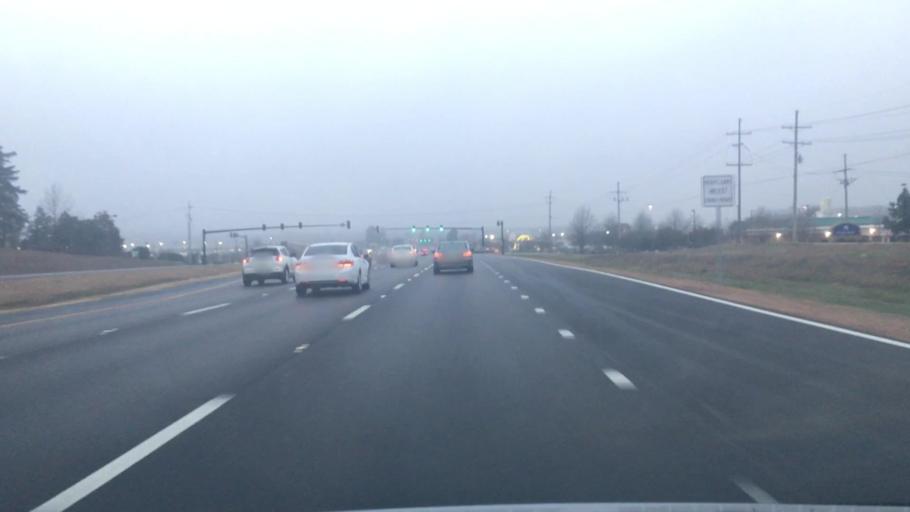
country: US
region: Mississippi
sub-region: Rankin County
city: Flowood
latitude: 32.3426
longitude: -90.0570
